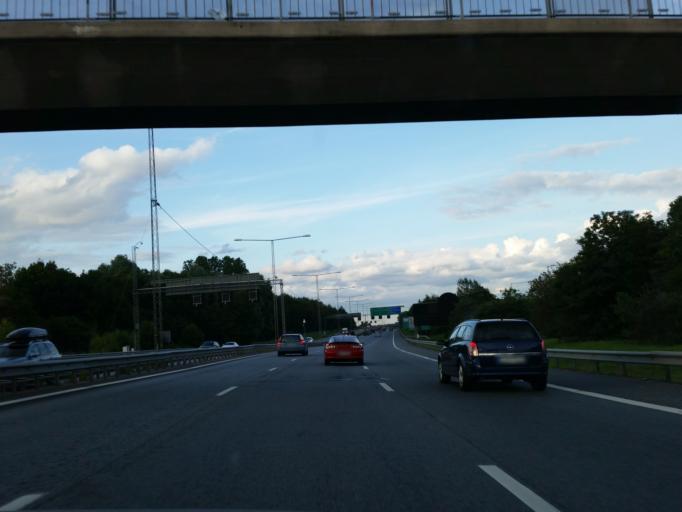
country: SE
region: Stockholm
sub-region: Botkyrka Kommun
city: Fittja
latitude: 59.2469
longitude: 17.8425
